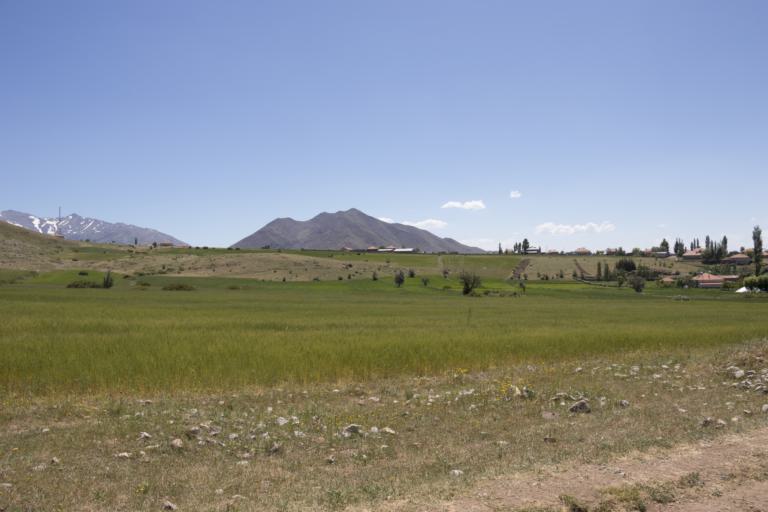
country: TR
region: Kayseri
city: Toklar
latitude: 38.4205
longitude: 36.1021
